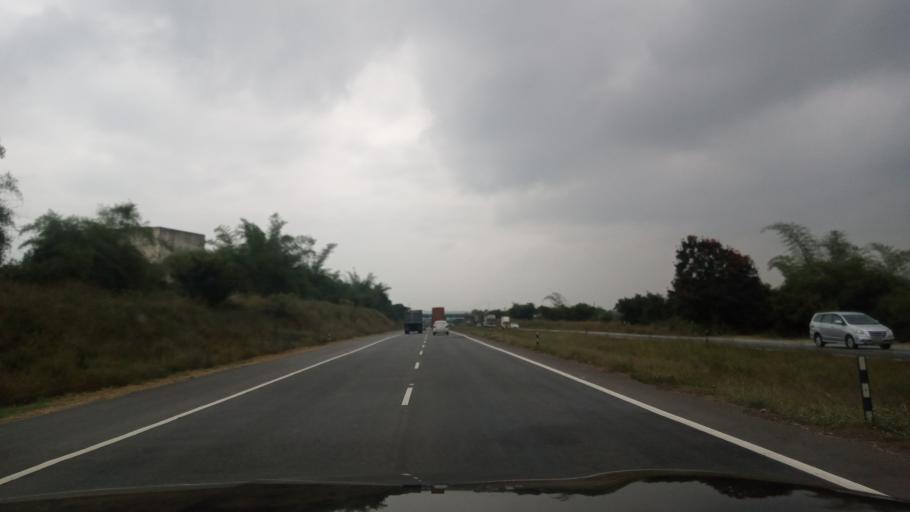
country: IN
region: Karnataka
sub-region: Bangalore Urban
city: Bangalore
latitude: 12.9660
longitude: 77.4715
